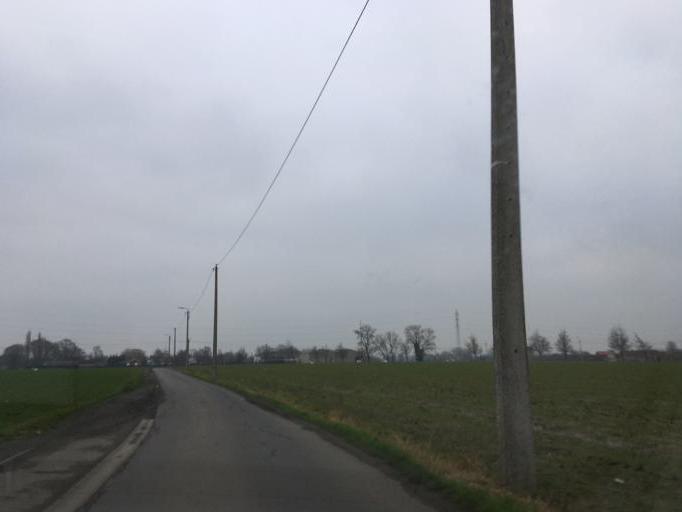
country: BE
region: Flanders
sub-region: Provincie West-Vlaanderen
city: Hooglede
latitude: 50.9699
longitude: 3.0916
